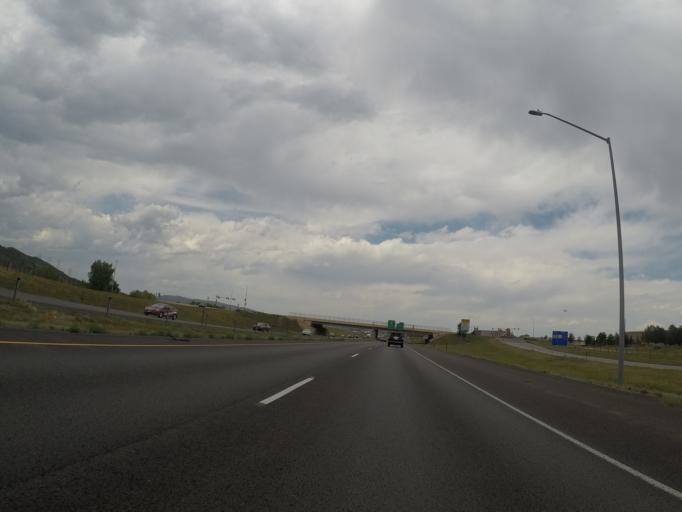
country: US
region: Colorado
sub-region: Jefferson County
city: Ken Caryl
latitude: 39.6077
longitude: -105.1532
